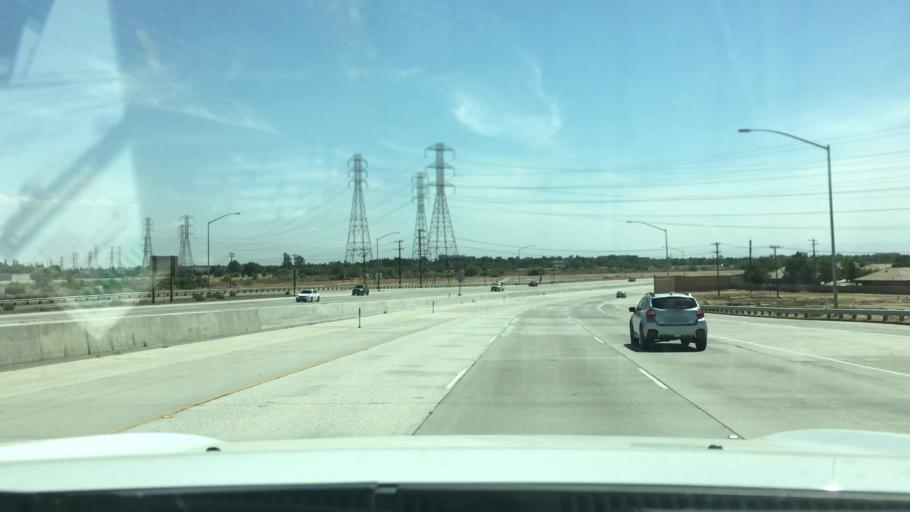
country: US
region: California
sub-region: Kern County
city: Greenacres
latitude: 35.3651
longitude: -119.0943
